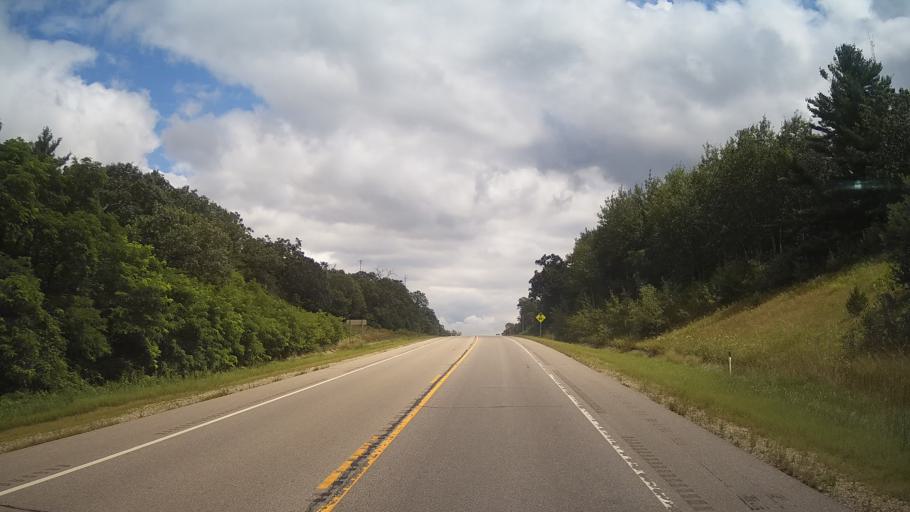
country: US
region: Wisconsin
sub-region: Marquette County
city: Westfield
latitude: 44.0218
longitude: -89.5728
